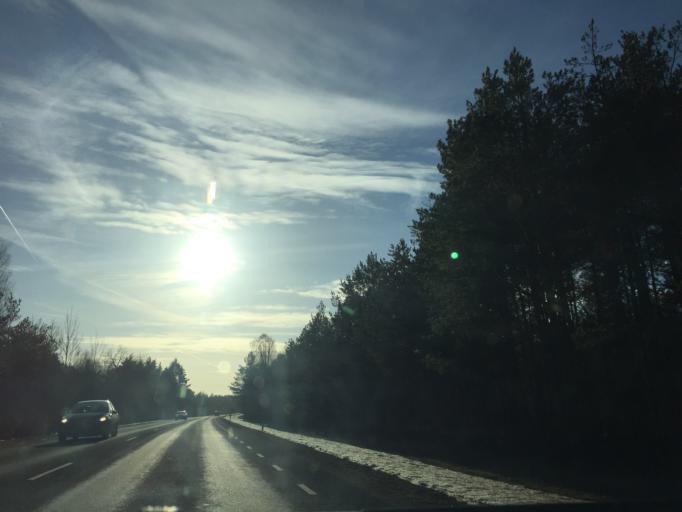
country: EE
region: Saare
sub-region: Orissaare vald
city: Orissaare
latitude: 58.4991
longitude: 22.8610
